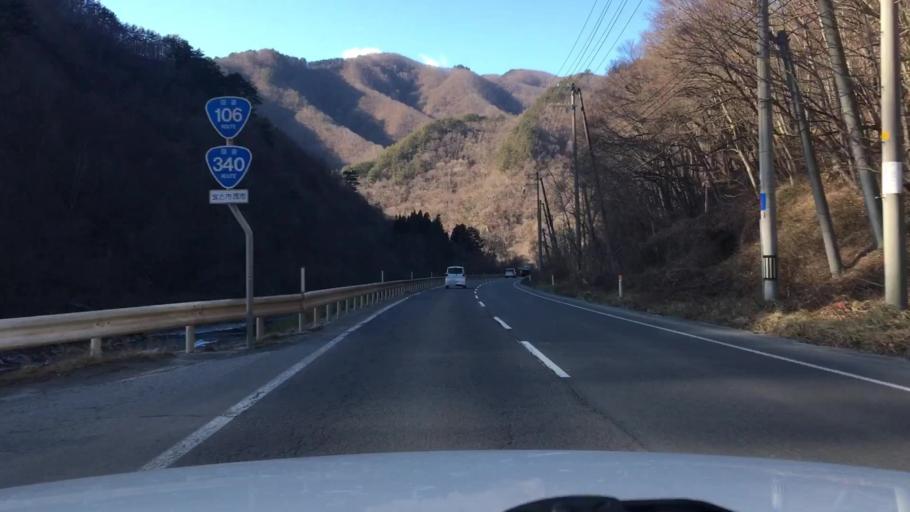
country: JP
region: Iwate
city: Miyako
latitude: 39.6071
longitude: 141.7821
